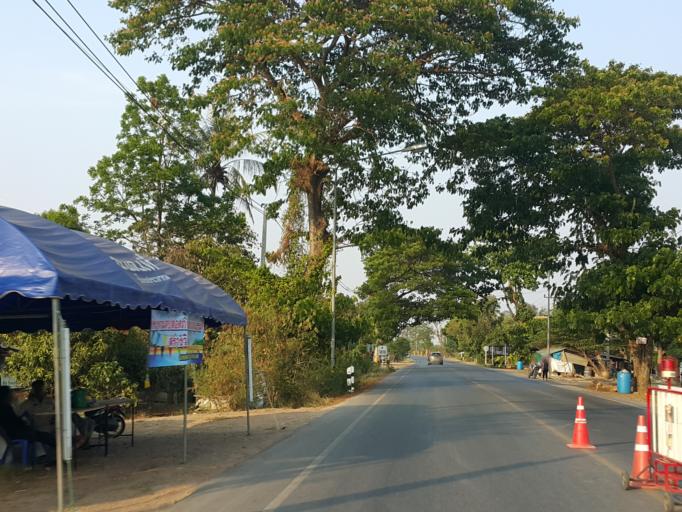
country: TH
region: Chai Nat
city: Sankhaburi
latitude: 15.0683
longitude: 100.1687
